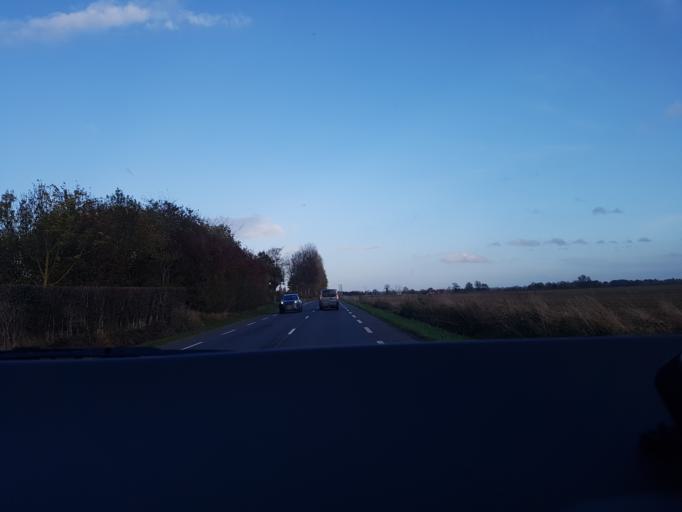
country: FR
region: Lower Normandy
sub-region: Departement du Calvados
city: Demouville
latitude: 49.1740
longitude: -0.2505
